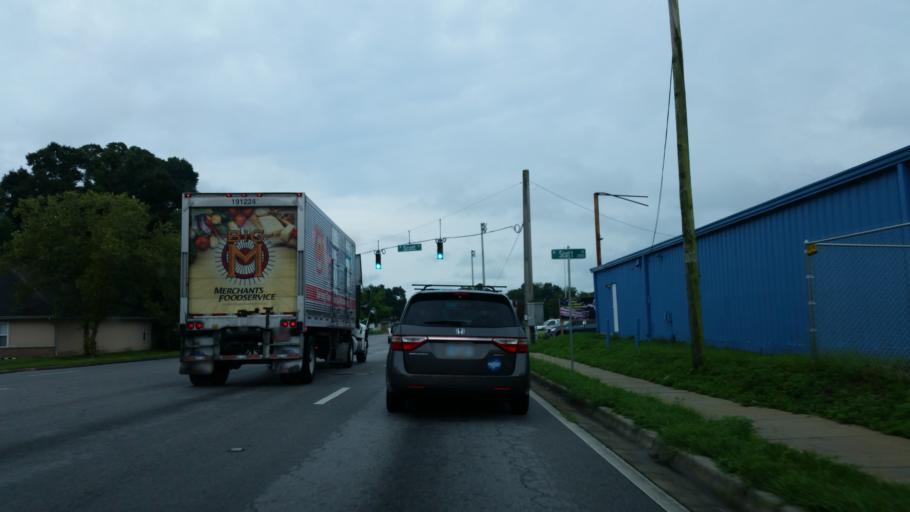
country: US
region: Florida
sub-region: Escambia County
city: Goulding
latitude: 30.4385
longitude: -87.2491
